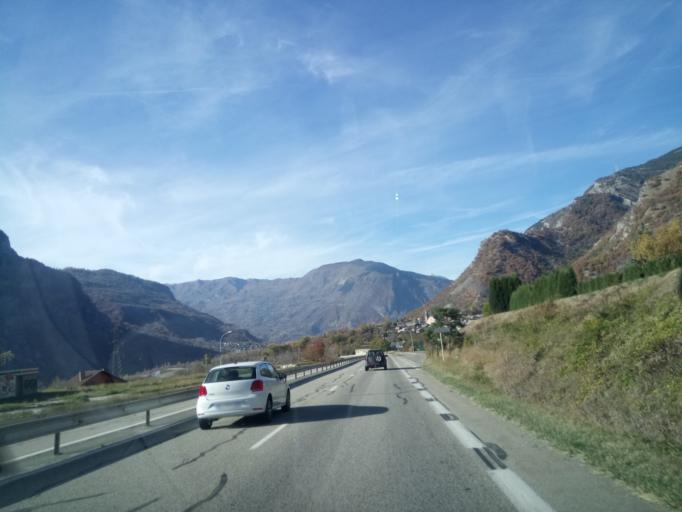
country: FR
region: Rhone-Alpes
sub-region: Departement de la Savoie
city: Villargondran
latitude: 45.2507
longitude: 6.4136
